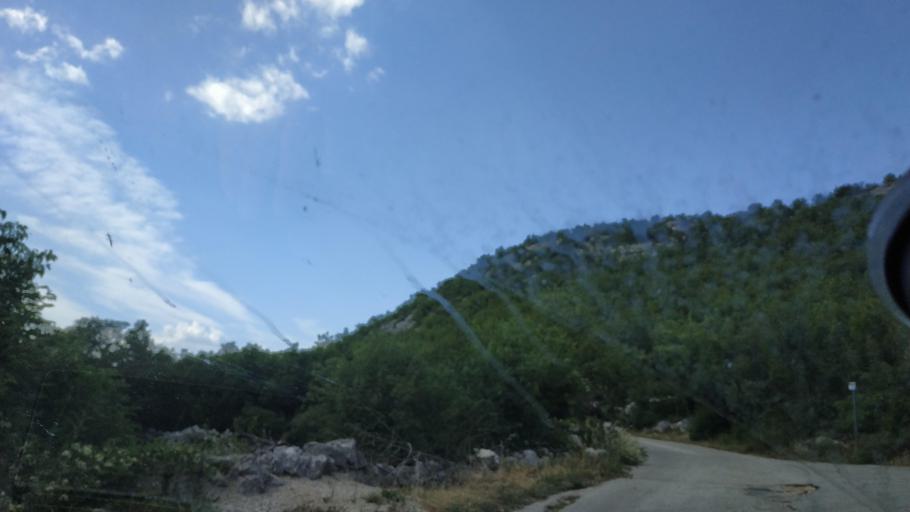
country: HR
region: Splitsko-Dalmatinska
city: Dugopolje
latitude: 43.5645
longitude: 16.6547
